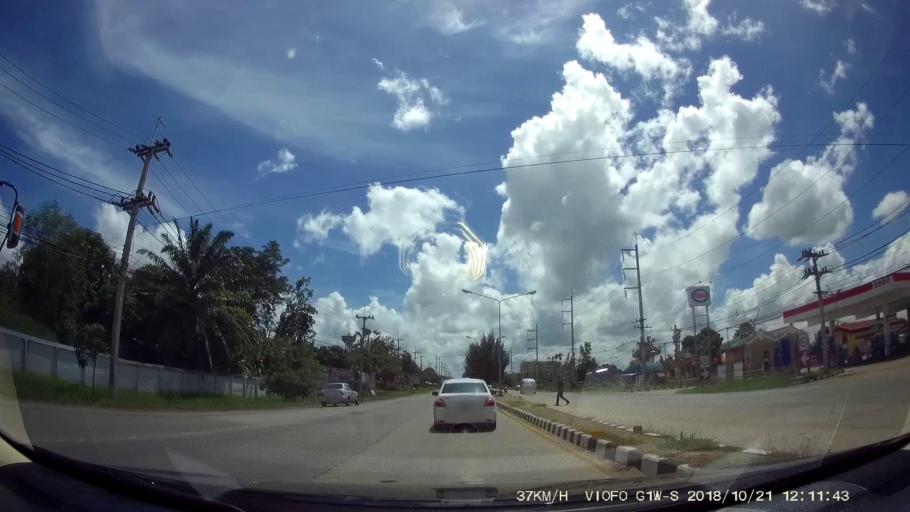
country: TH
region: Chaiyaphum
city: Chatturat
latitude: 15.4135
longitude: 101.8337
